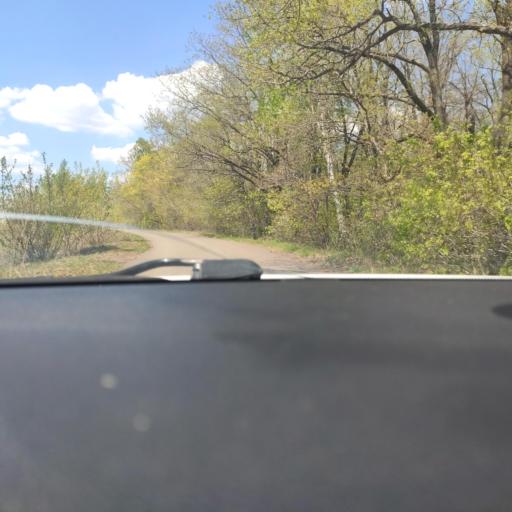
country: RU
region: Bashkortostan
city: Avdon
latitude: 54.6125
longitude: 55.6220
